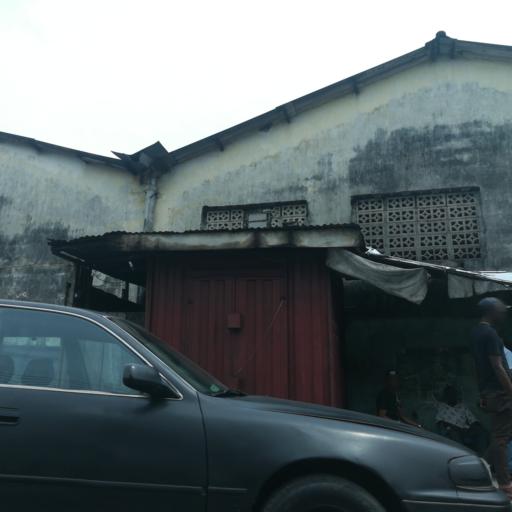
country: NG
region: Rivers
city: Port Harcourt
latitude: 4.8059
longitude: 7.0082
